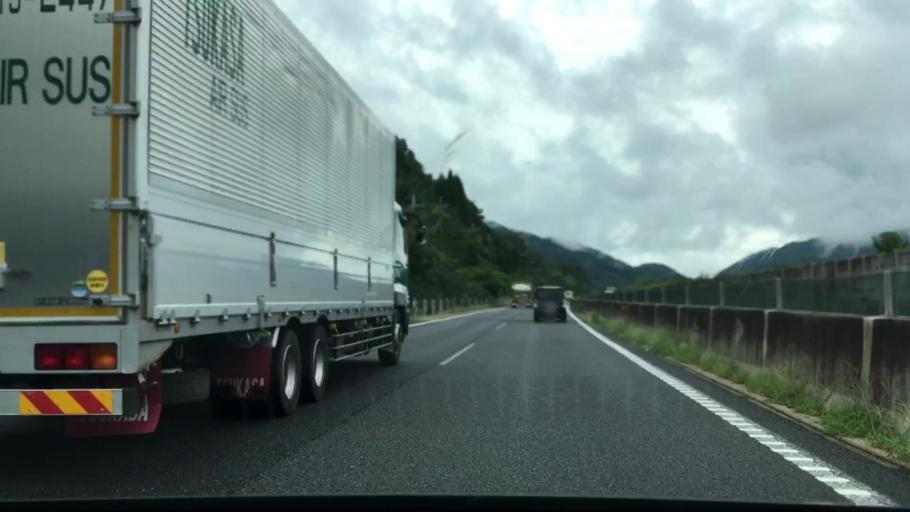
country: JP
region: Hyogo
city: Yamazakicho-nakabirose
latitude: 35.0161
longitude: 134.5090
